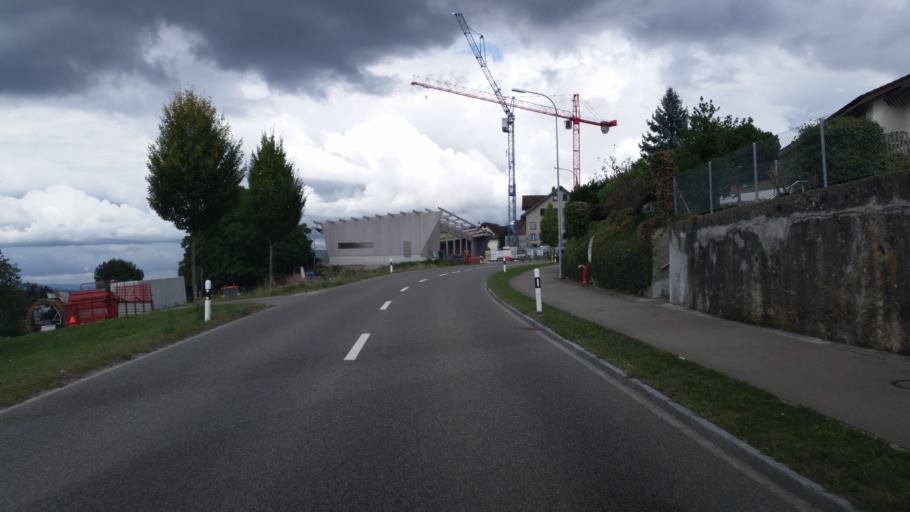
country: CH
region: Aargau
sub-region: Bezirk Bremgarten
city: Oberlunkhofen
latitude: 47.3092
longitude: 8.3902
